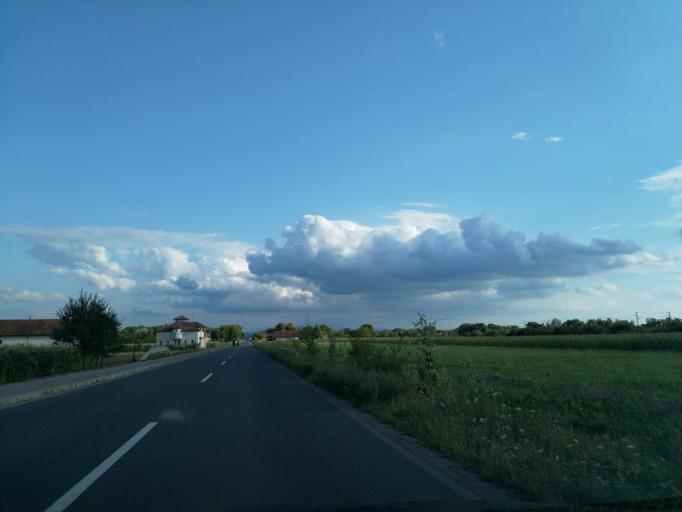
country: RS
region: Central Serbia
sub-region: Pomoravski Okrug
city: Paracin
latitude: 43.8093
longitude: 21.4206
